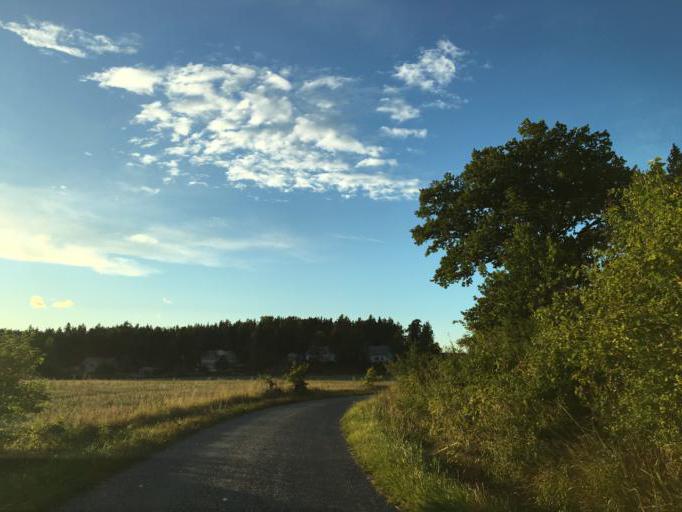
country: SE
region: Soedermanland
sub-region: Eskilstuna Kommun
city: Torshalla
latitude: 59.4329
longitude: 16.4514
